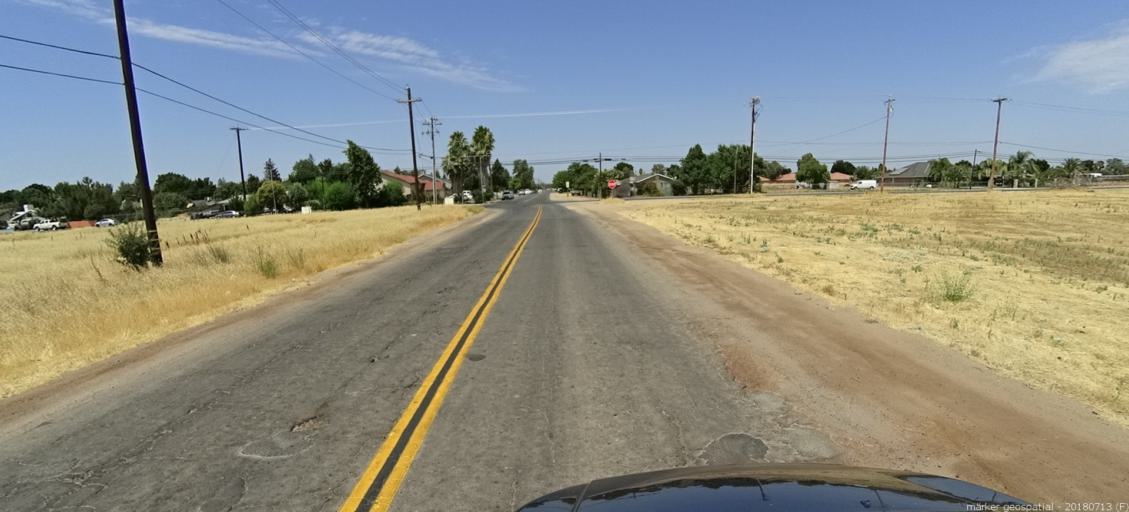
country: US
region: California
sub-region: Madera County
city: Madera
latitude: 36.9829
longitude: -120.0622
